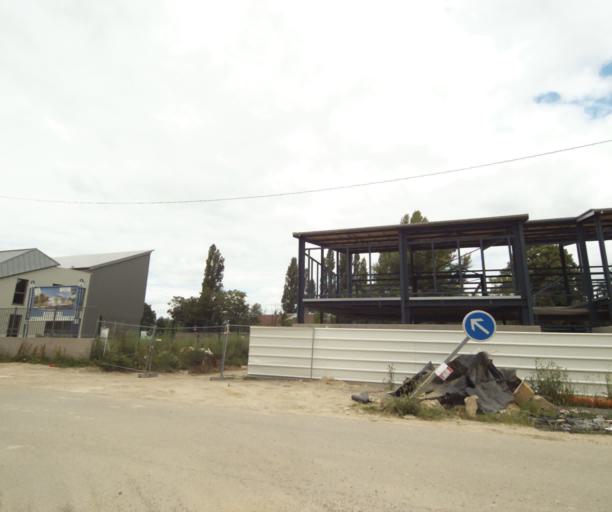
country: FR
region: Ile-de-France
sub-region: Departement des Yvelines
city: Saint-Cyr-l'Ecole
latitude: 48.8080
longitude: 2.0682
